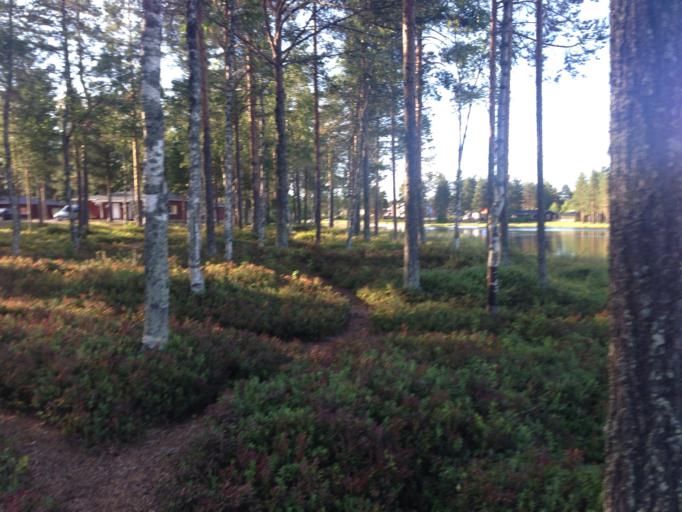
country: SE
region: Norrbotten
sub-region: Arvidsjaurs Kommun
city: Arvidsjaur
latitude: 65.5814
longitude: 19.1988
